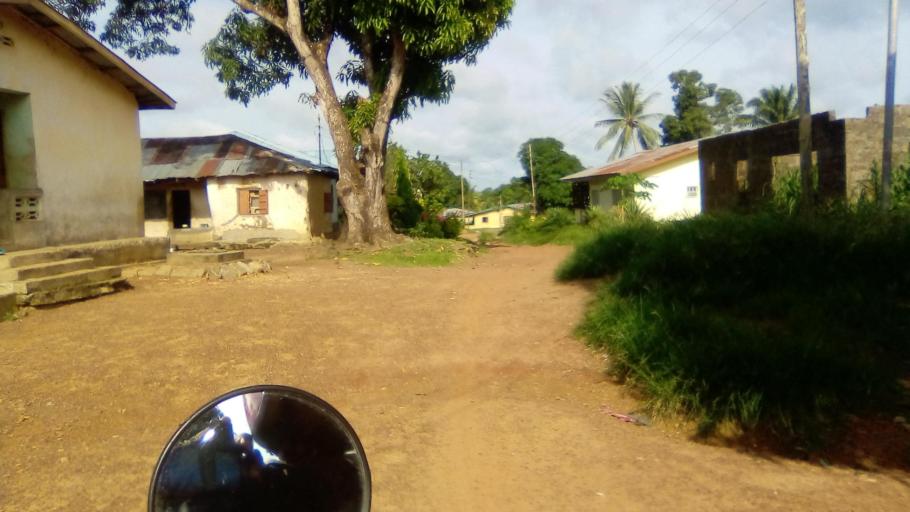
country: SL
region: Southern Province
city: Bo
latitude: 7.9561
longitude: -11.7609
